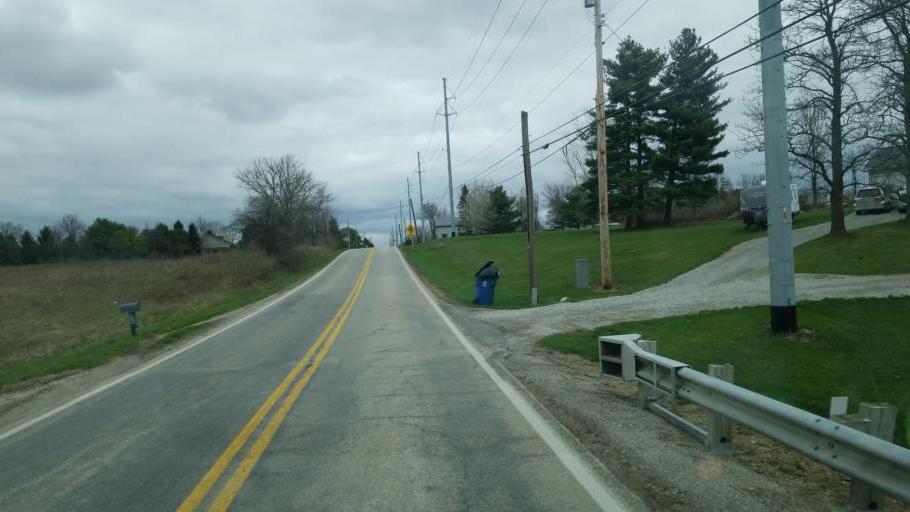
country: US
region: Ohio
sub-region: Delaware County
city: Delaware
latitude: 40.3477
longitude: -83.0989
